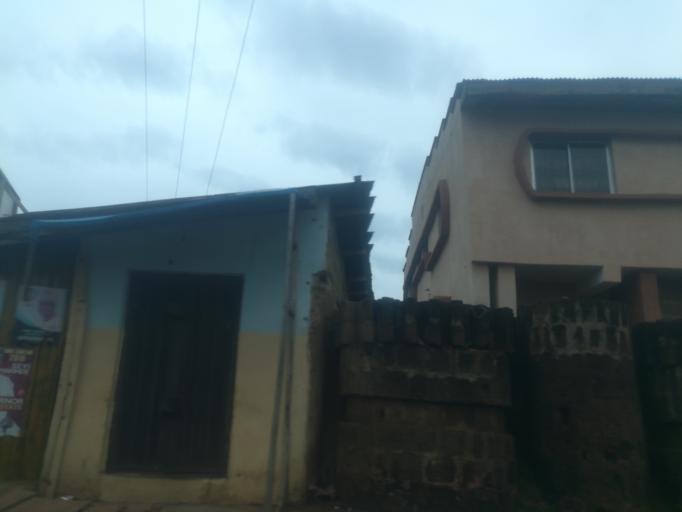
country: NG
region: Oyo
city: Egbeda
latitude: 7.4052
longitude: 3.9787
